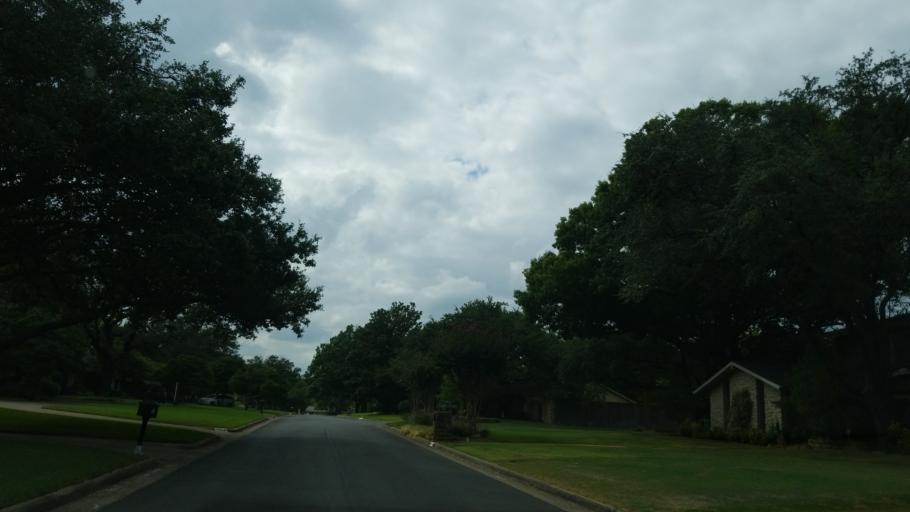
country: US
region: Texas
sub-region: Dallas County
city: Addison
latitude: 32.9429
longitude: -96.7814
